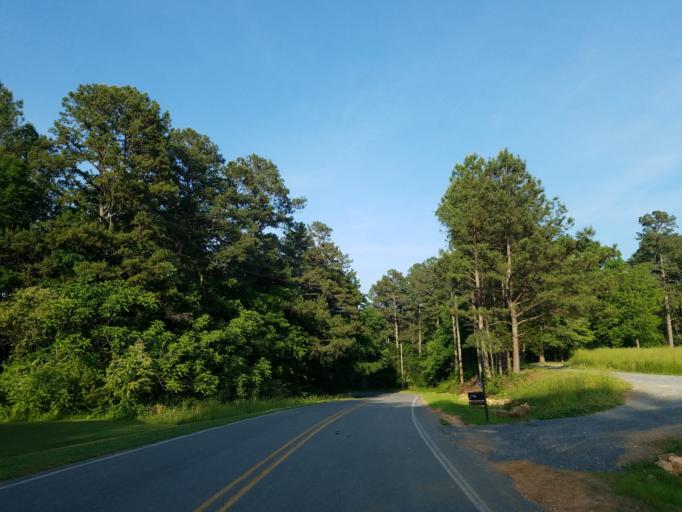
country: US
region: Georgia
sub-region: Floyd County
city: Shannon
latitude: 34.4880
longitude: -85.1302
